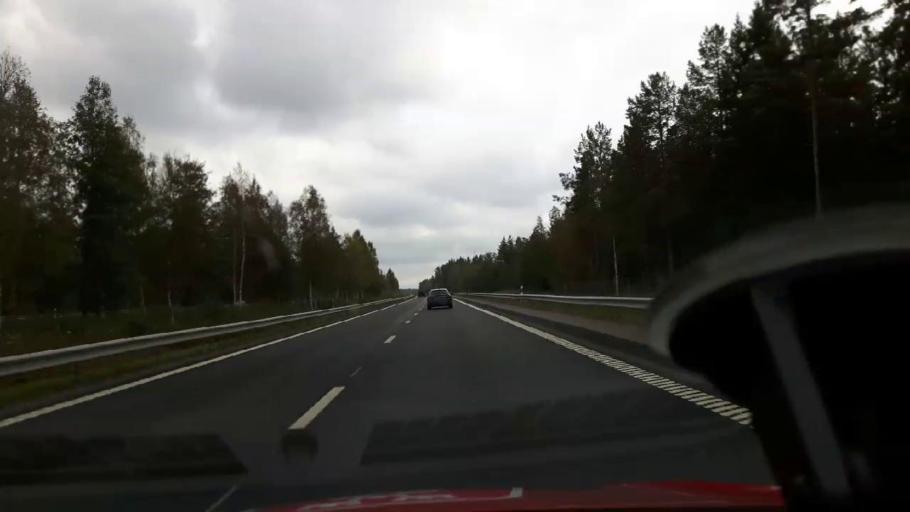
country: SE
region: Gaevleborg
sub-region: Gavle Kommun
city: Gavle
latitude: 60.6195
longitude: 17.1611
